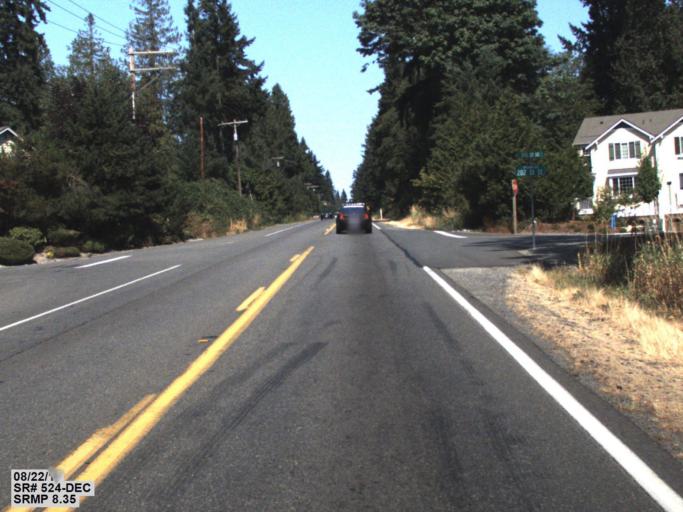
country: US
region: Washington
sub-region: Snohomish County
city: Martha Lake
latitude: 47.8144
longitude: -122.2282
